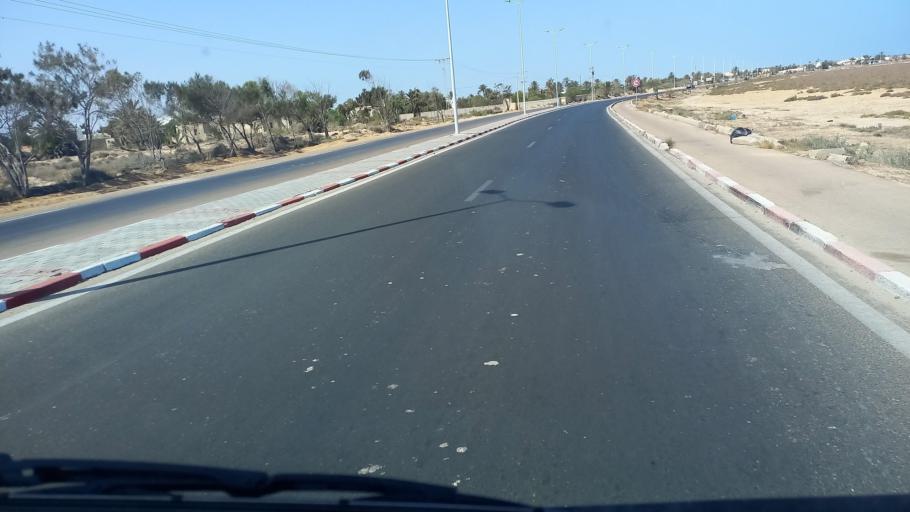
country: TN
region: Madanin
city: Midoun
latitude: 33.8688
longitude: 10.9449
